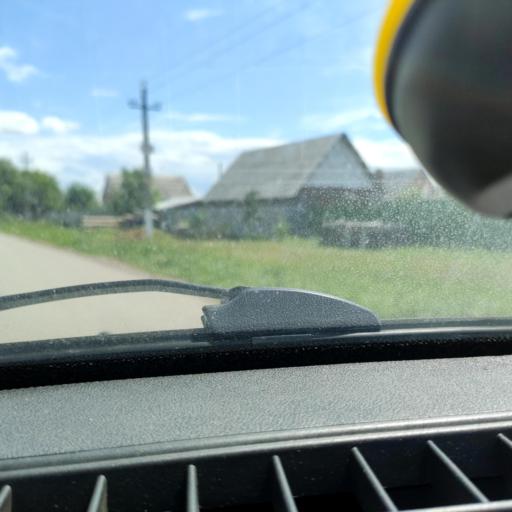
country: RU
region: Samara
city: Zhigulevsk
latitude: 53.5503
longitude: 49.5219
